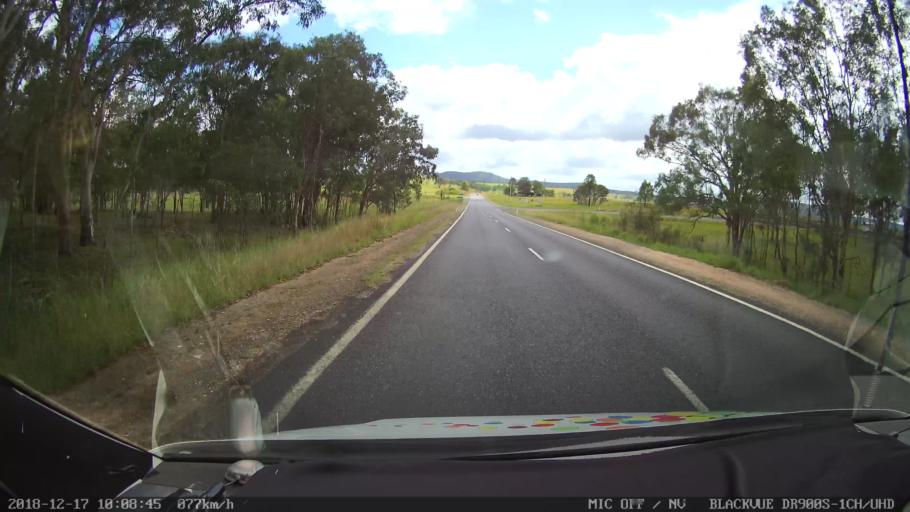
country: AU
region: New South Wales
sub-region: Tenterfield Municipality
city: Carrolls Creek
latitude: -28.8900
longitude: 152.5354
